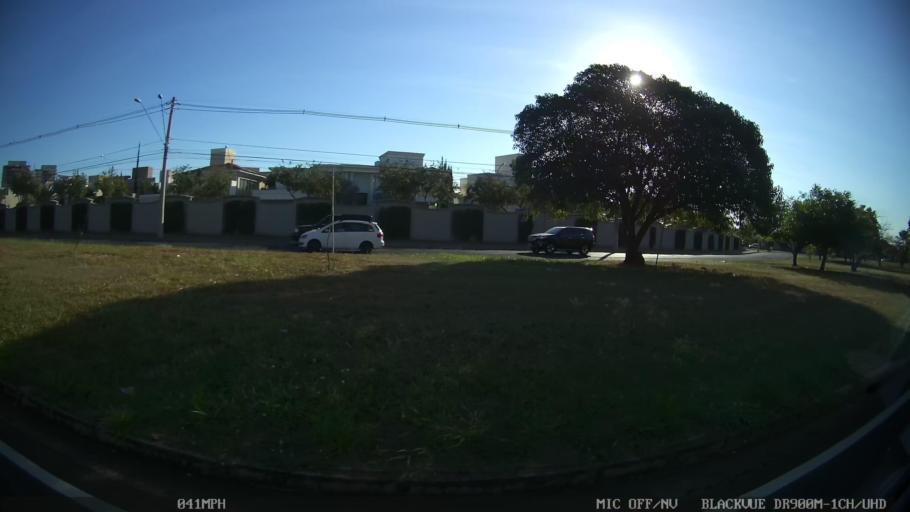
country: BR
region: Sao Paulo
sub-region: Sao Jose Do Rio Preto
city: Sao Jose do Rio Preto
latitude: -20.8607
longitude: -49.4118
